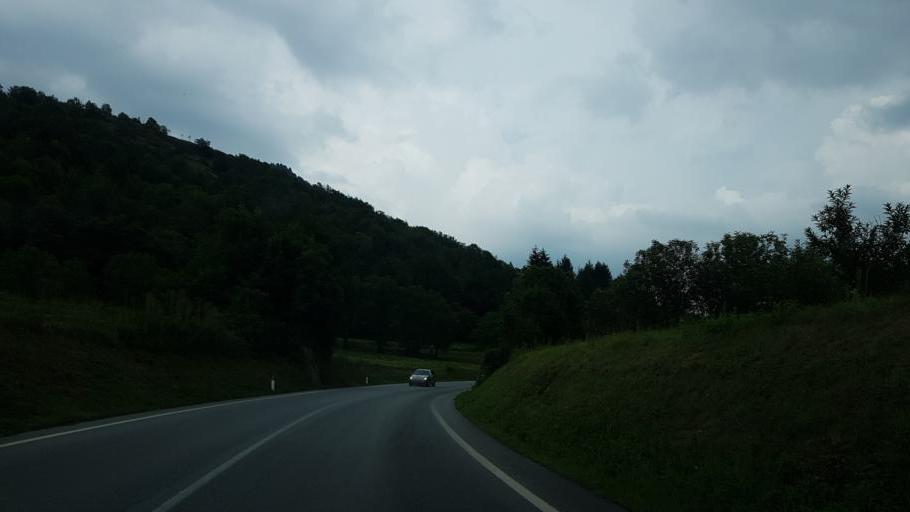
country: IT
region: Piedmont
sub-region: Provincia di Cuneo
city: Moiola
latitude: 44.3313
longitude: 7.3965
